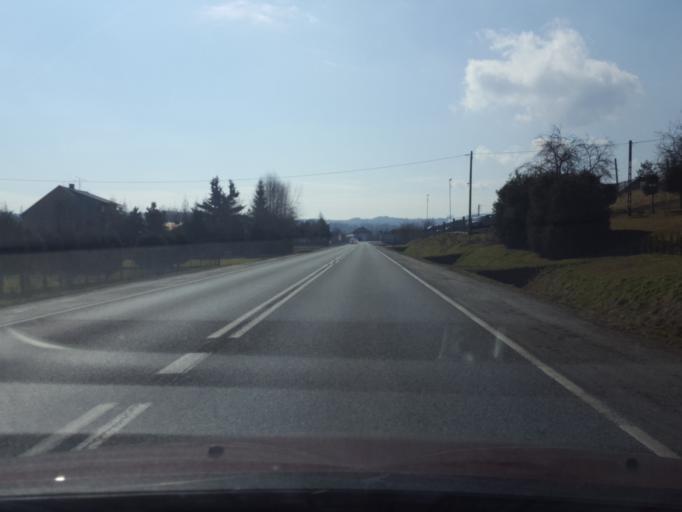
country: PL
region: Lesser Poland Voivodeship
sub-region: Powiat nowosadecki
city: Lososina Dolna
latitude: 49.7600
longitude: 20.6347
